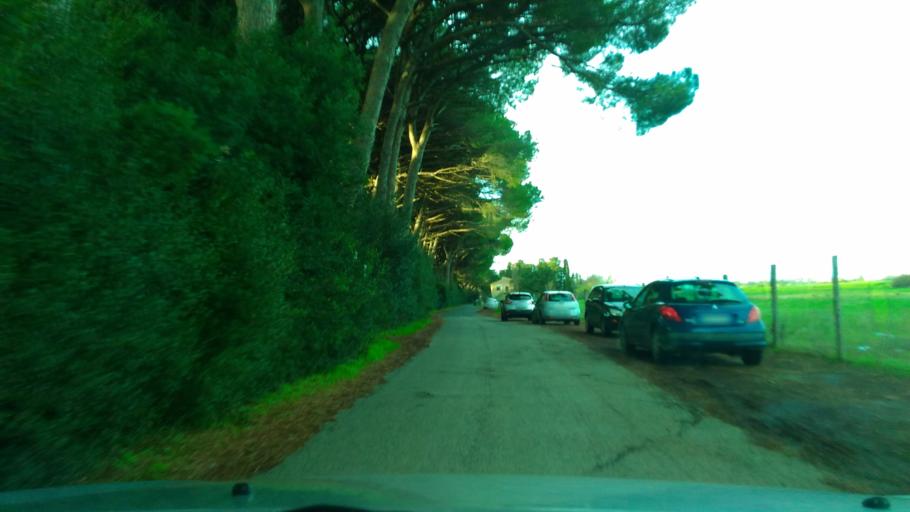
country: IT
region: Tuscany
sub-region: Provincia di Livorno
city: Cecina
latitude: 43.2800
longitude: 10.5141
